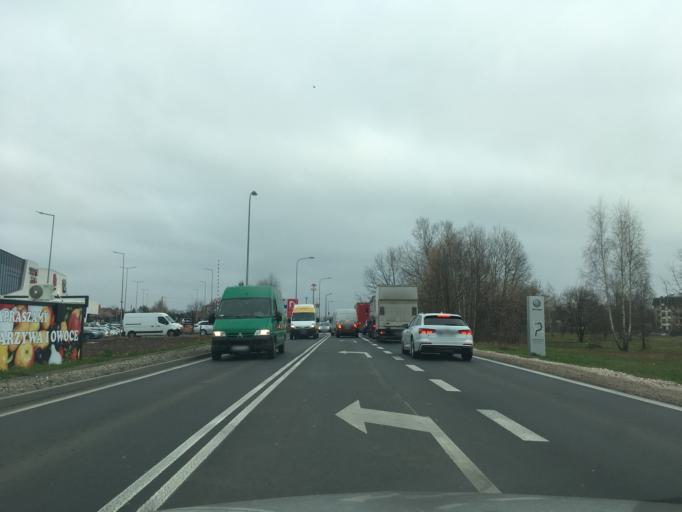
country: PL
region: Masovian Voivodeship
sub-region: Powiat piaseczynski
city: Piaseczno
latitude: 52.0821
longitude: 21.0103
